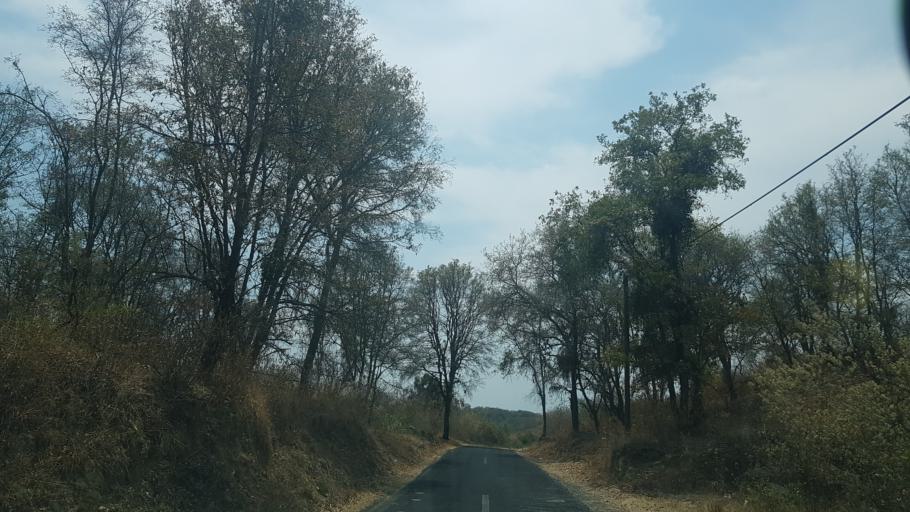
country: MX
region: Puebla
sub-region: Tochimilco
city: La Magdalena Yancuitlalpan
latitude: 18.8776
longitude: -98.5992
